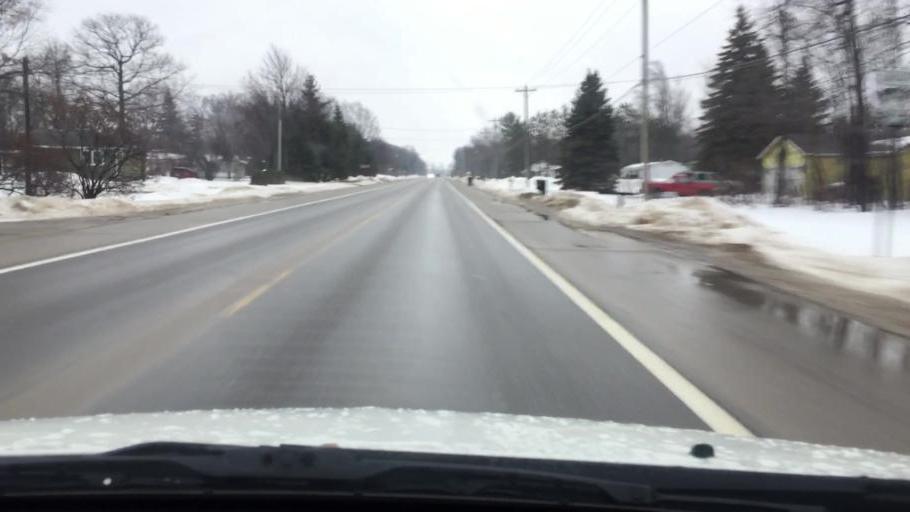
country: US
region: Michigan
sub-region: Charlevoix County
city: Charlevoix
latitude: 45.2921
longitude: -85.2497
